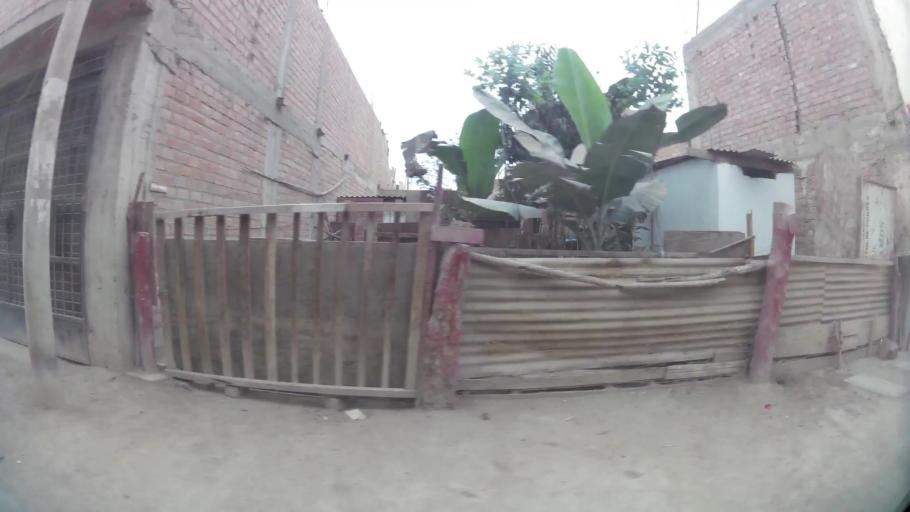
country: PE
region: Lima
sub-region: Lima
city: Independencia
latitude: -11.9629
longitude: -77.0968
